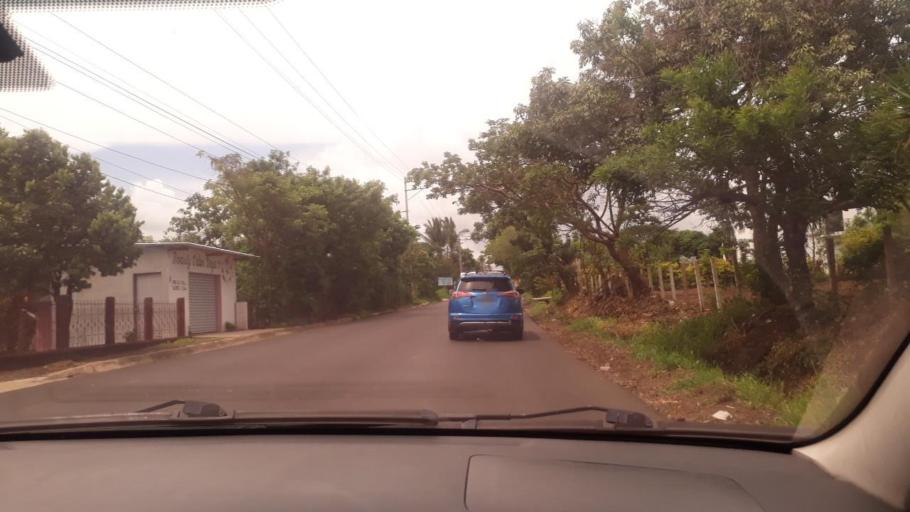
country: GT
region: Jutiapa
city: Quesada
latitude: 14.2594
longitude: -90.0230
